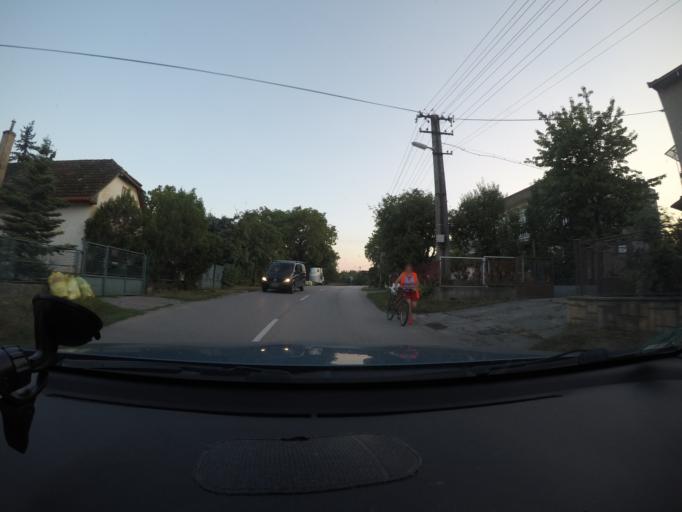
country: SK
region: Trenciansky
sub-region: Okres Trencin
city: Trencin
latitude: 48.8695
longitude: 17.9487
